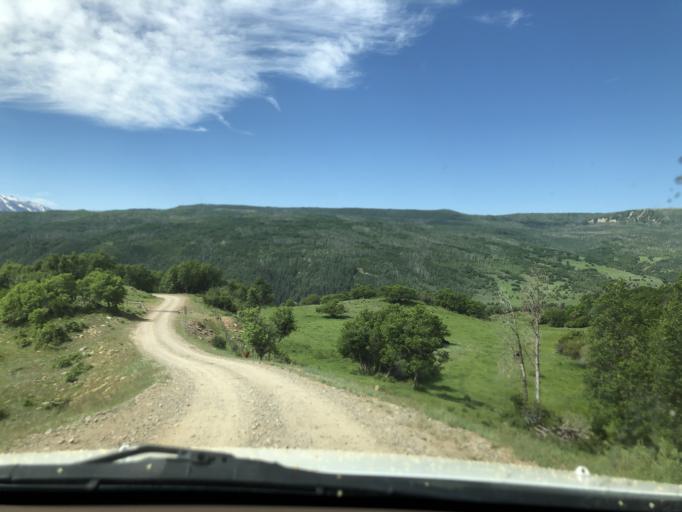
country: US
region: Colorado
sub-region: Delta County
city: Paonia
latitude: 39.0025
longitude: -107.3456
